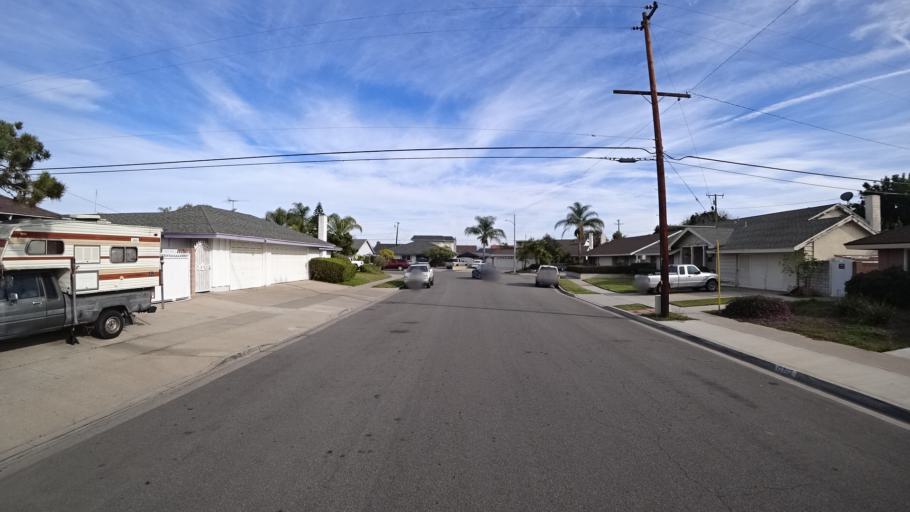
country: US
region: California
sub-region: Orange County
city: Garden Grove
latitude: 33.7712
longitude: -117.9062
